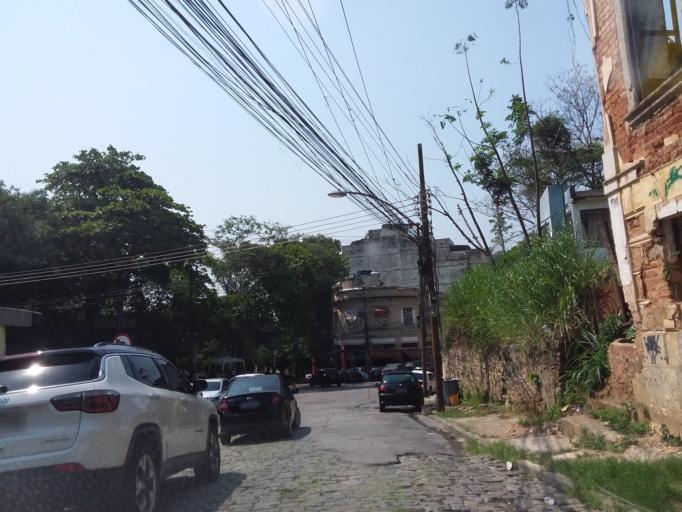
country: BR
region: Rio de Janeiro
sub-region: Rio De Janeiro
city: Rio de Janeiro
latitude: -22.9320
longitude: -43.2086
